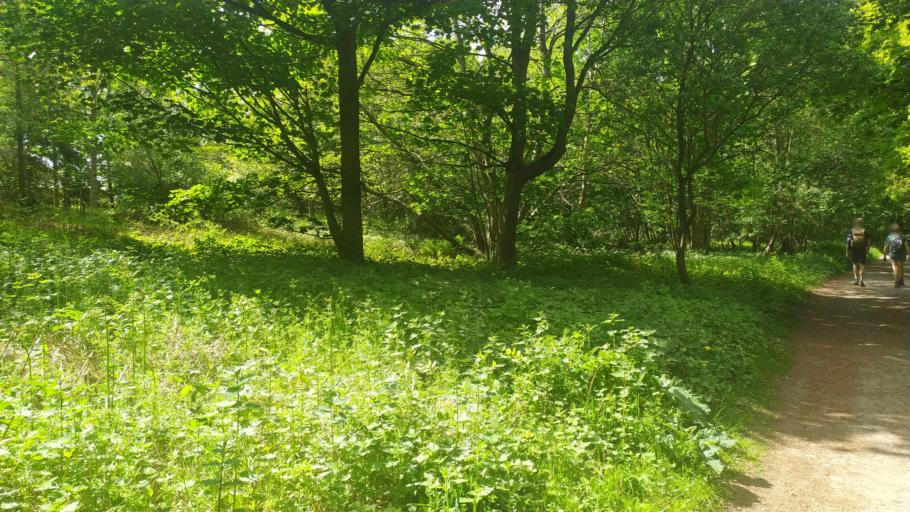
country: GB
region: England
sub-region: City and Borough of Leeds
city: Chapel Allerton
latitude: 53.8886
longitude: -1.5384
